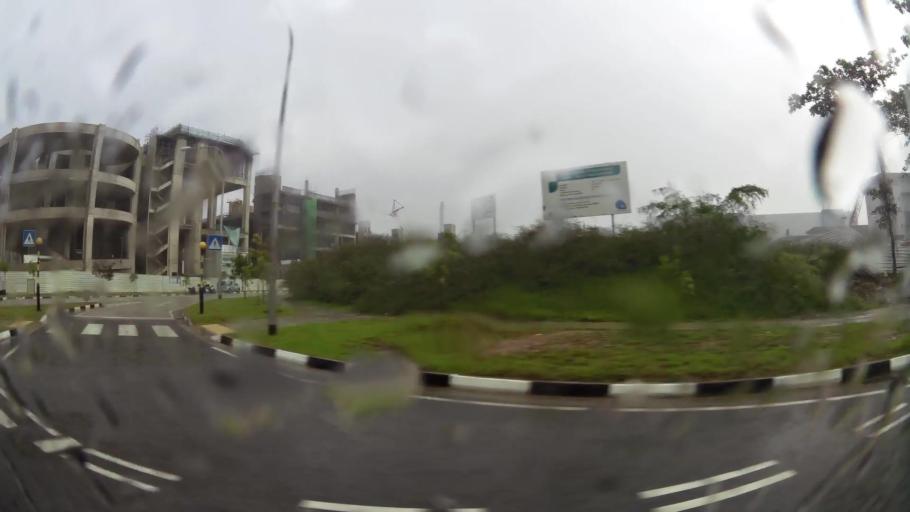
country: MY
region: Johor
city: Kampung Pasir Gudang Baru
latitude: 1.3774
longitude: 103.9199
